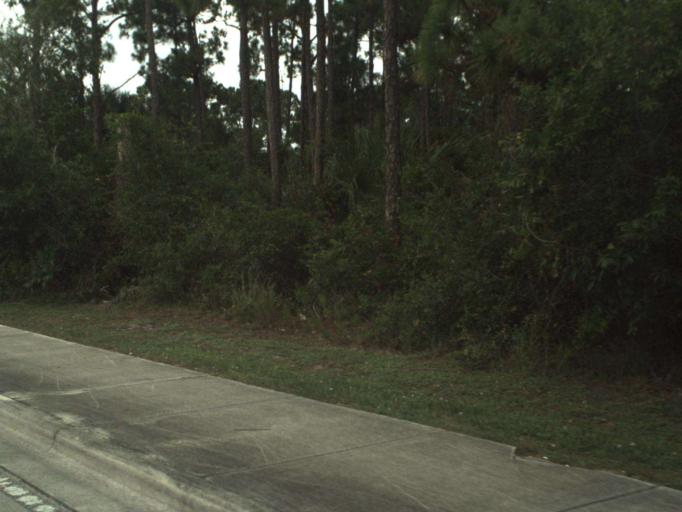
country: US
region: Florida
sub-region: Saint Lucie County
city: White City
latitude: 27.3680
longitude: -80.3504
